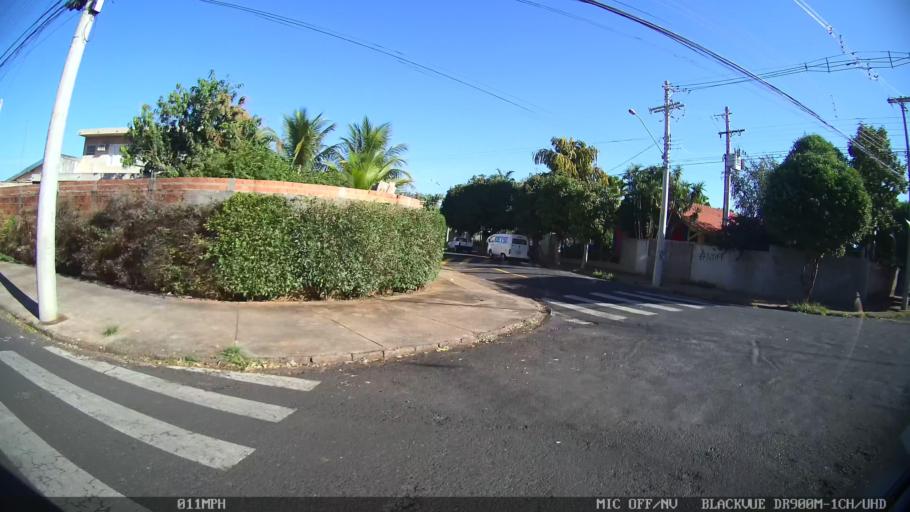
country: BR
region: Sao Paulo
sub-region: Olimpia
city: Olimpia
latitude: -20.7402
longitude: -48.8959
